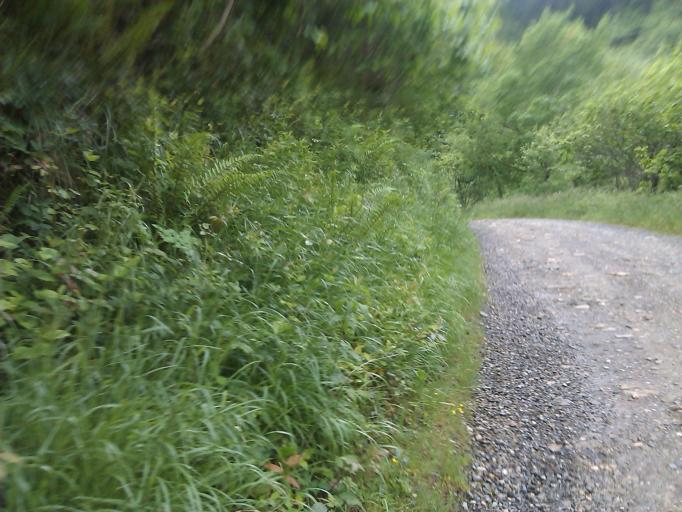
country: ES
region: Basque Country
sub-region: Provincia de Guipuzcoa
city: Elduayen
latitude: 43.1743
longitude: -1.9852
